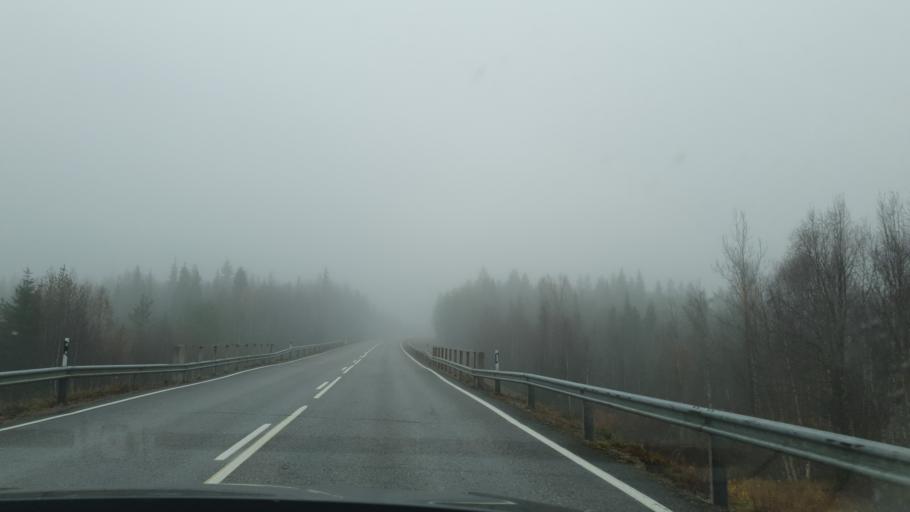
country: FI
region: Lapland
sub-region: Tunturi-Lappi
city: Kittilae
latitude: 67.2138
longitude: 24.9267
